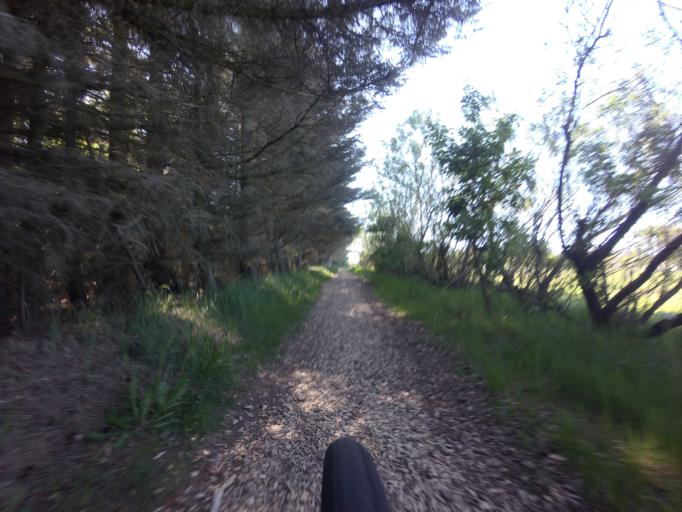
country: DK
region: North Denmark
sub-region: Jammerbugt Kommune
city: Pandrup
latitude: 57.2559
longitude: 9.6197
